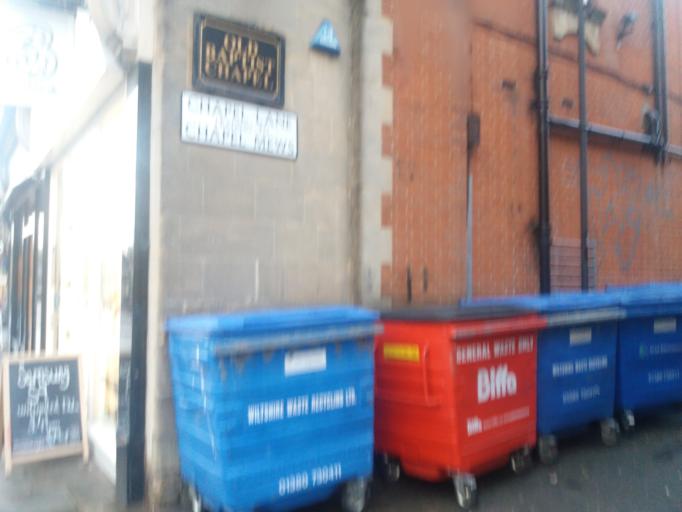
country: GB
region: England
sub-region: Wiltshire
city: Chippenham
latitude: 51.4584
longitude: -2.1150
